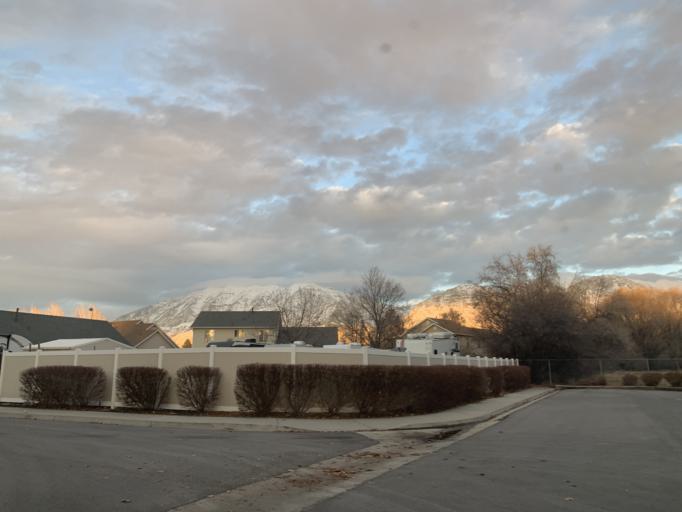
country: US
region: Utah
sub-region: Utah County
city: Provo
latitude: 40.2384
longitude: -111.7004
